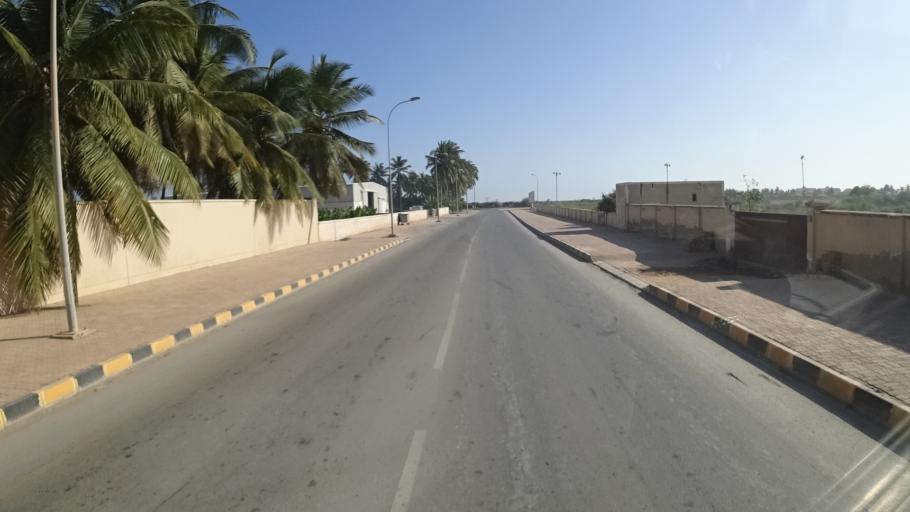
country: OM
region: Zufar
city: Salalah
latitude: 17.0033
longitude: 54.0687
